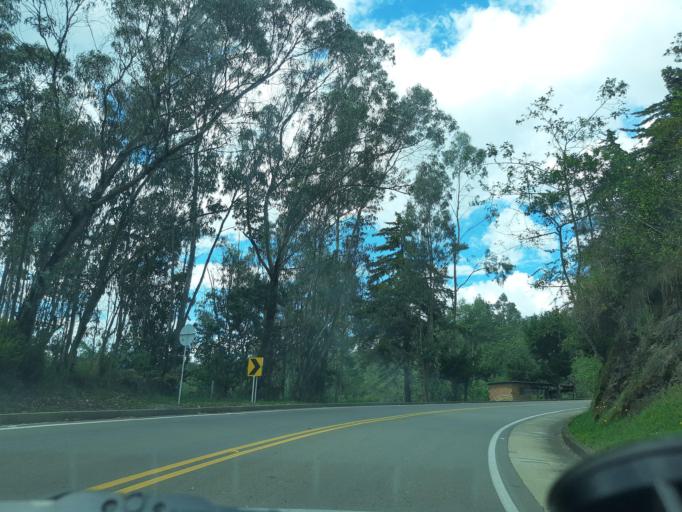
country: CO
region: Boyaca
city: Raquira
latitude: 5.5872
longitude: -73.7048
